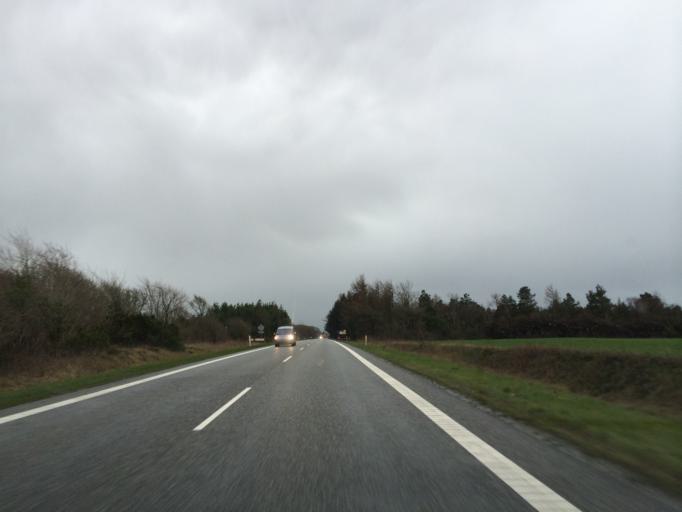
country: DK
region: Central Jutland
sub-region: Ringkobing-Skjern Kommune
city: Tarm
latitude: 55.8114
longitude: 8.4922
